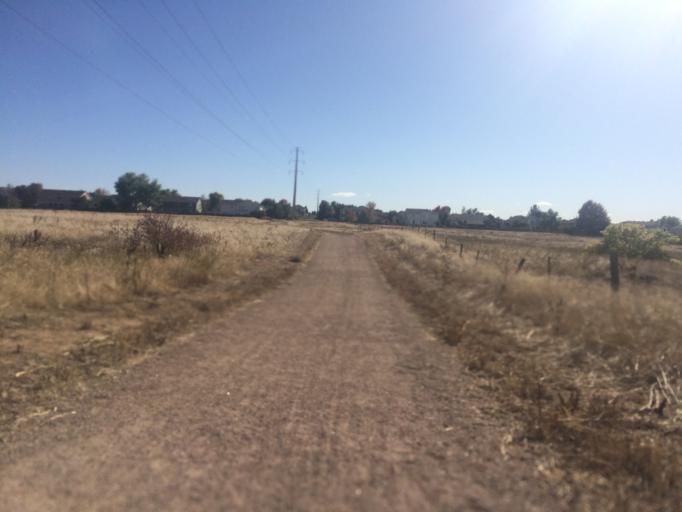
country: US
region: Colorado
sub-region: Broomfield County
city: Broomfield
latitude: 39.8800
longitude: -105.0720
